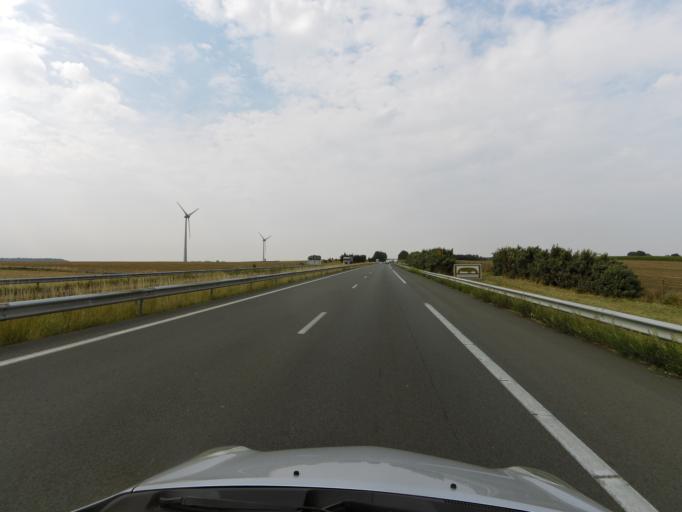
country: FR
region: Picardie
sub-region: Departement de l'Aisne
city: Holnon
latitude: 49.9407
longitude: 3.2136
